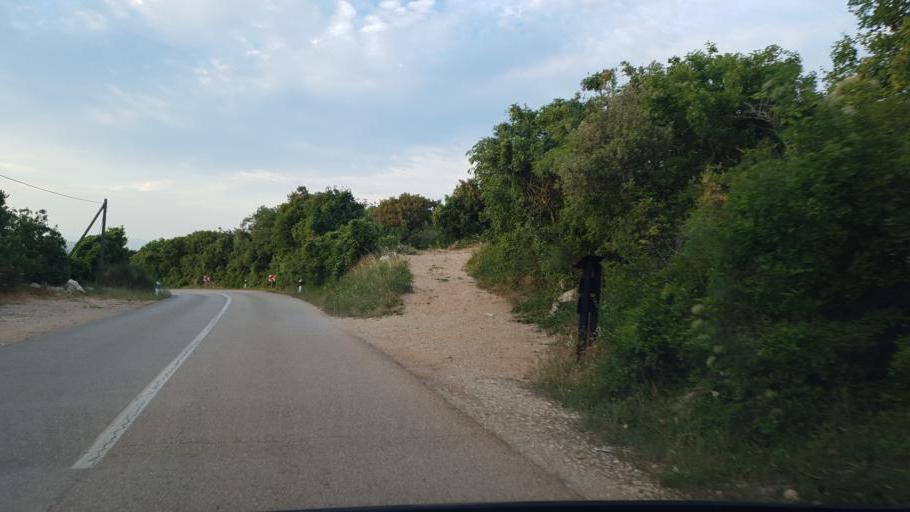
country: HR
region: Primorsko-Goranska
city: Punat
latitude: 45.0040
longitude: 14.6338
